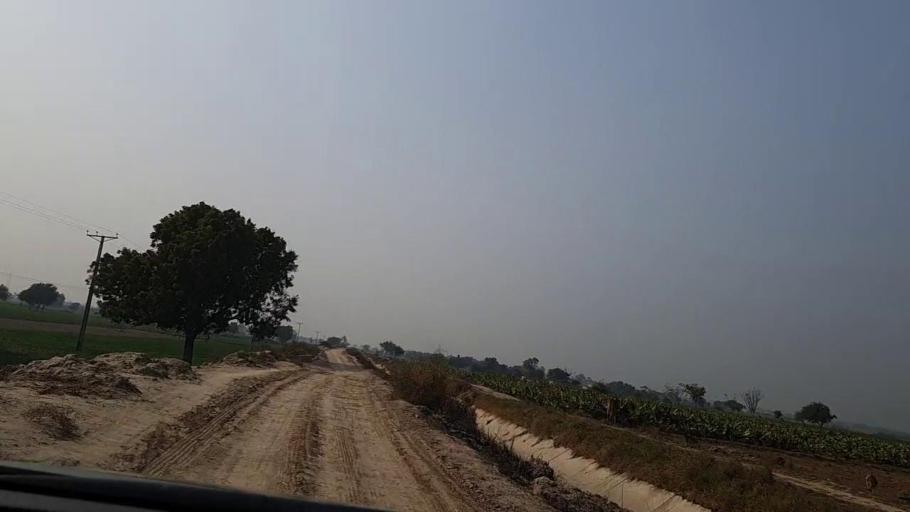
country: PK
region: Sindh
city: Sakrand
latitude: 26.1391
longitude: 68.2296
